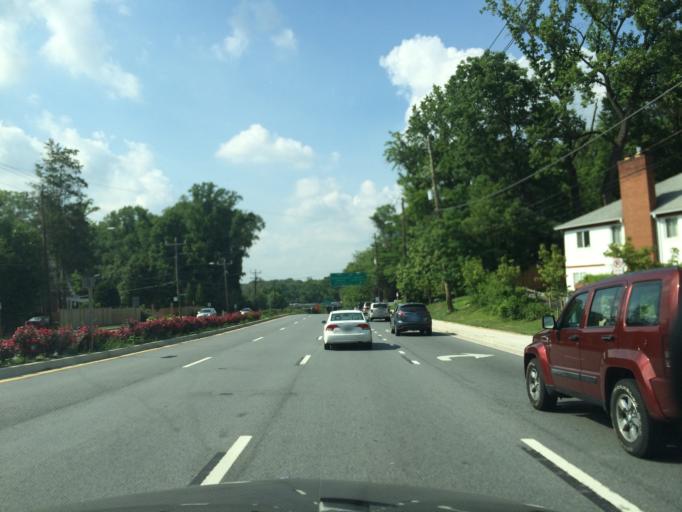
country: US
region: Maryland
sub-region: Montgomery County
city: South Kensington
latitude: 39.0013
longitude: -77.0771
